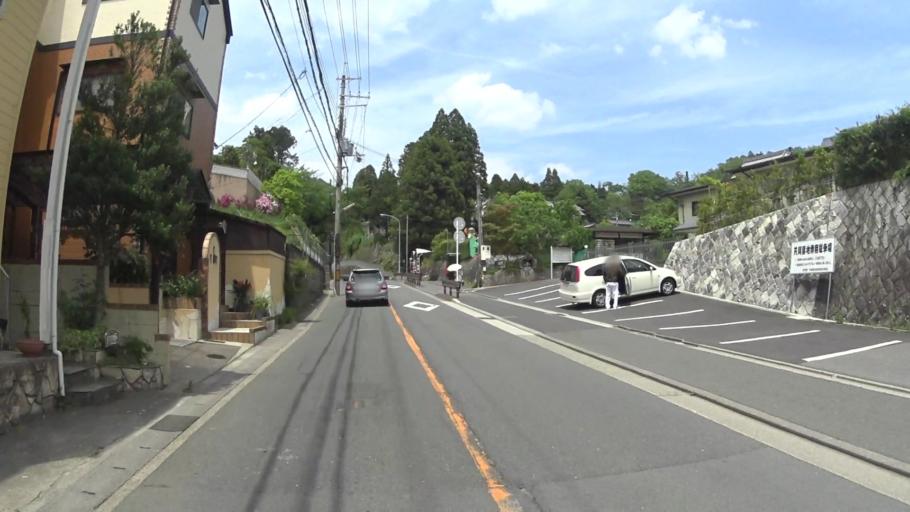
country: JP
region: Kyoto
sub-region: Kyoto-shi
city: Kamigyo-ku
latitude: 35.0839
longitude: 135.7617
